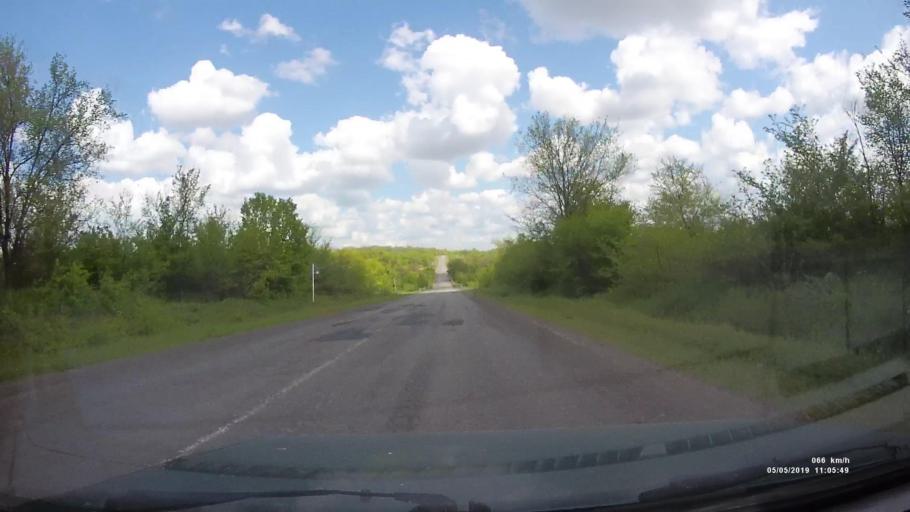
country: RU
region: Rostov
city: Ust'-Donetskiy
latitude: 47.7095
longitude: 40.9113
